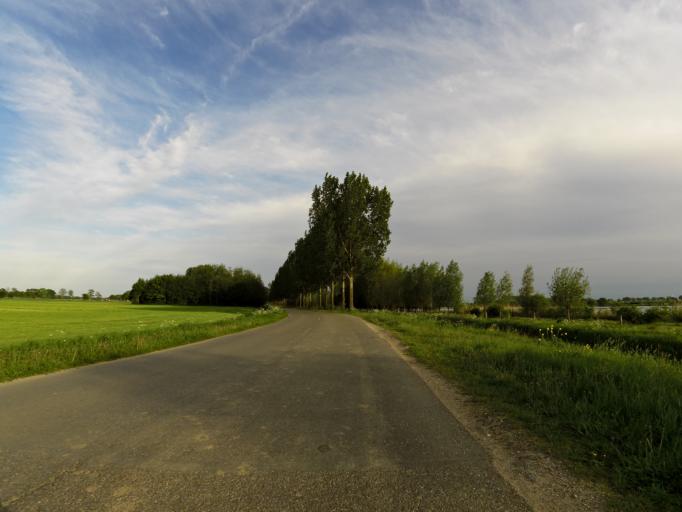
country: NL
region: Gelderland
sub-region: Oude IJsselstreek
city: Gendringen
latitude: 51.8839
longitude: 6.3338
